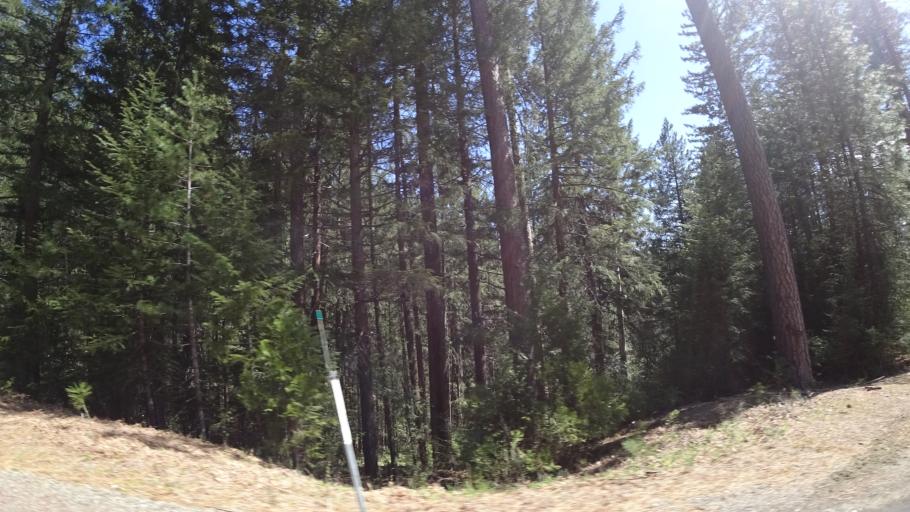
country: US
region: California
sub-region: Trinity County
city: Lewiston
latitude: 40.8975
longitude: -122.7879
